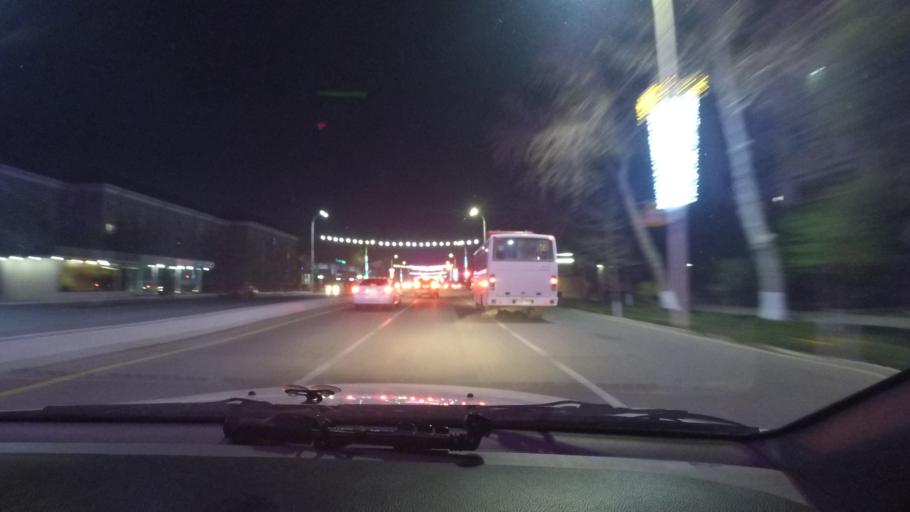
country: UZ
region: Bukhara
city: Bukhara
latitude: 39.7715
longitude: 64.4427
